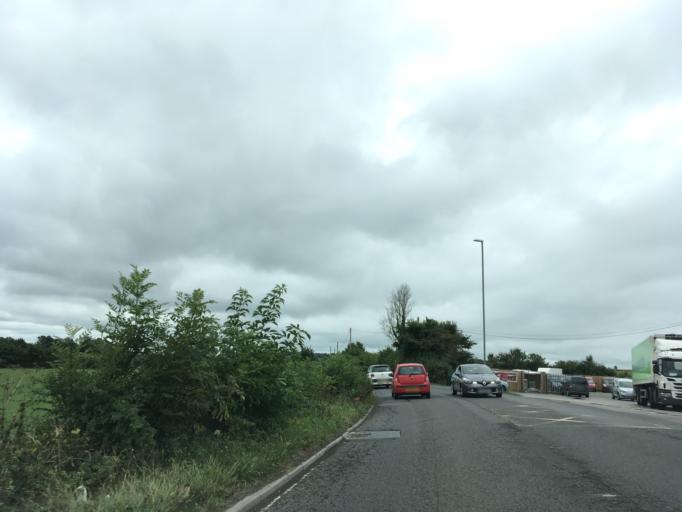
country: GB
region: England
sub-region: Bath and North East Somerset
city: Timsbury
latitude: 51.3567
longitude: -2.4844
